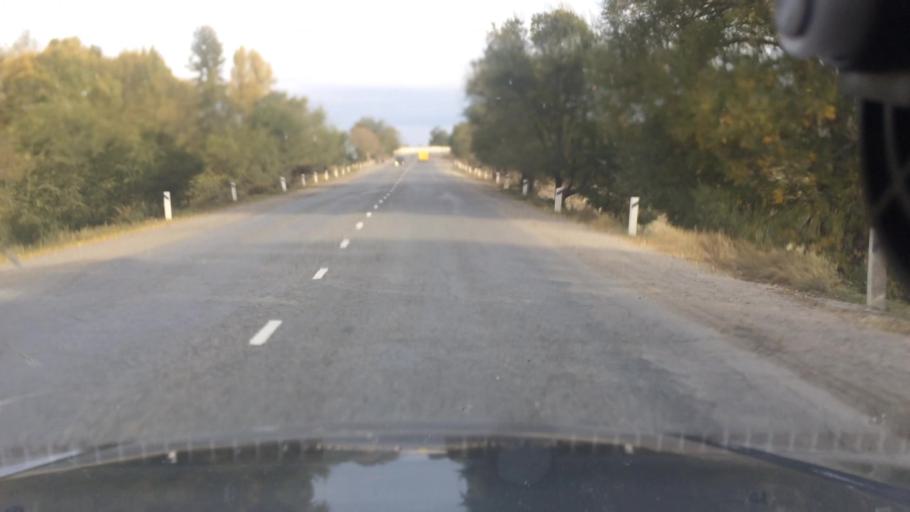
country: KG
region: Ysyk-Koel
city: Karakol
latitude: 42.5339
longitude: 78.3818
